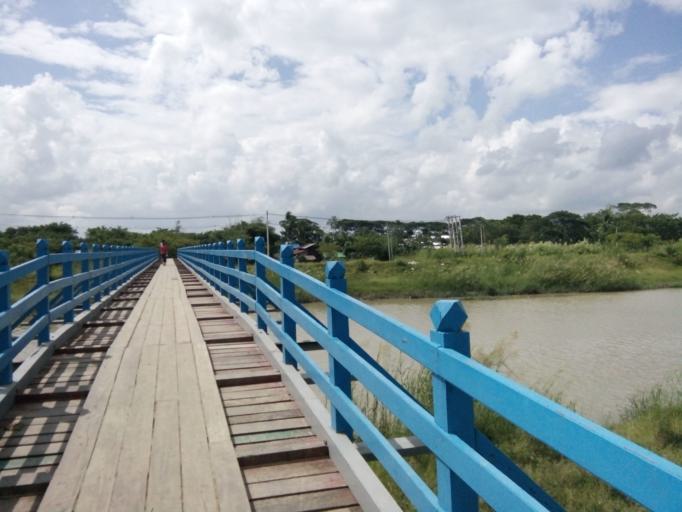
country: MM
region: Yangon
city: Kanbe
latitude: 16.8715
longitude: 95.9815
